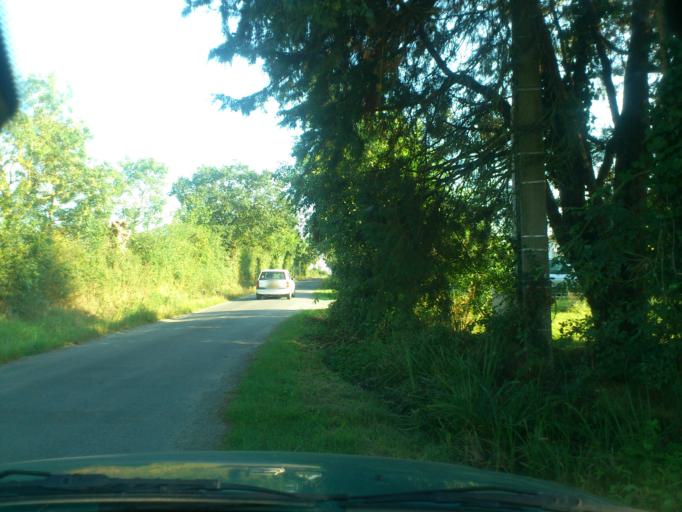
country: FR
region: Pays de la Loire
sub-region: Departement de la Loire-Atlantique
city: Saint-Hilaire-de-Clisson
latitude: 47.0332
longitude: -1.3053
